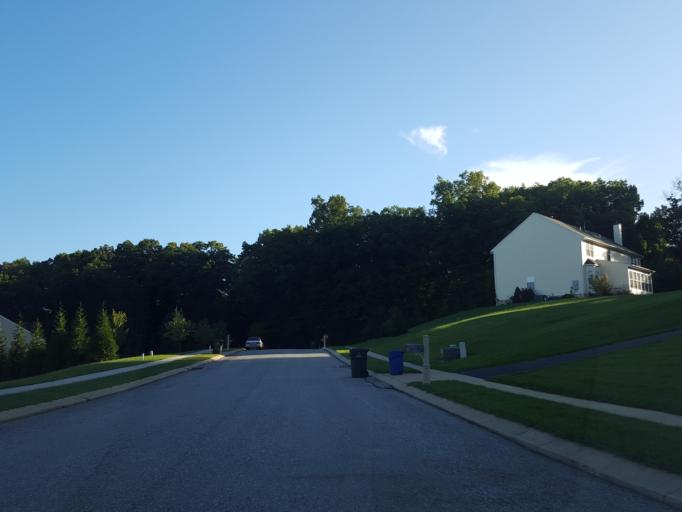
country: US
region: Pennsylvania
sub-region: York County
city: Windsor
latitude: 39.9447
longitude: -76.6020
